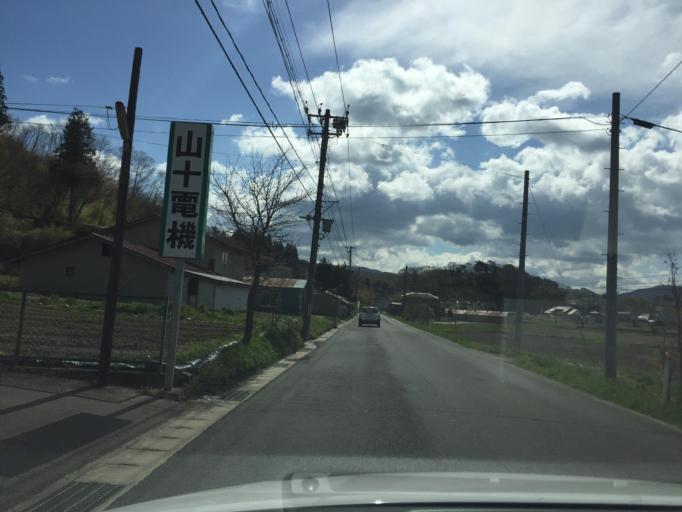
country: JP
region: Fukushima
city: Funehikimachi-funehiki
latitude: 37.6072
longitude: 140.6680
